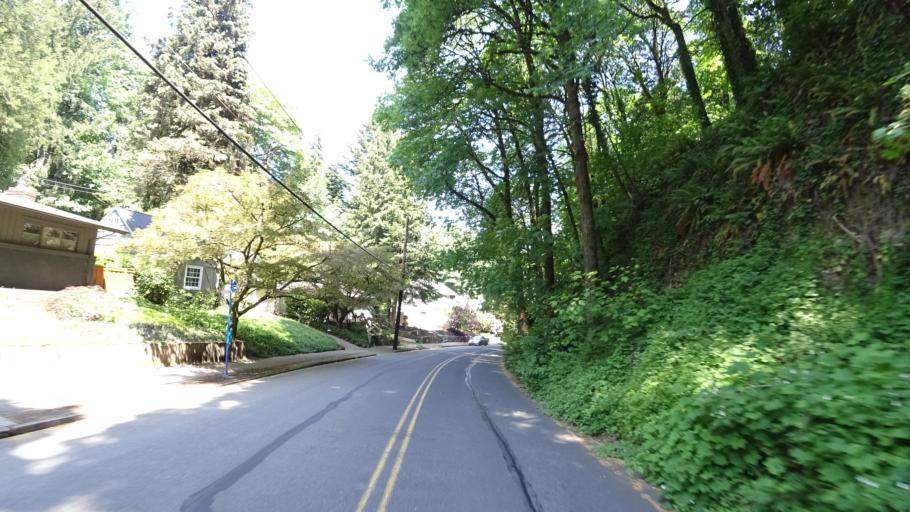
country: US
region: Oregon
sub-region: Multnomah County
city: Portland
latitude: 45.5187
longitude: -122.7120
